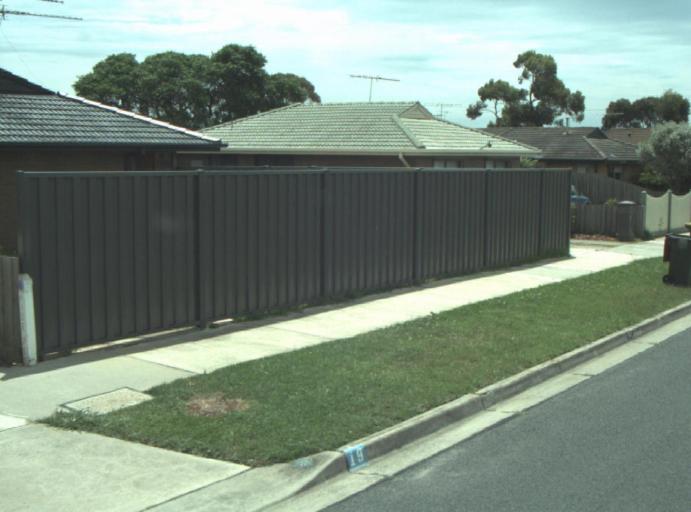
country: AU
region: Victoria
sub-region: Greater Geelong
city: Leopold
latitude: -38.1890
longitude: 144.4739
